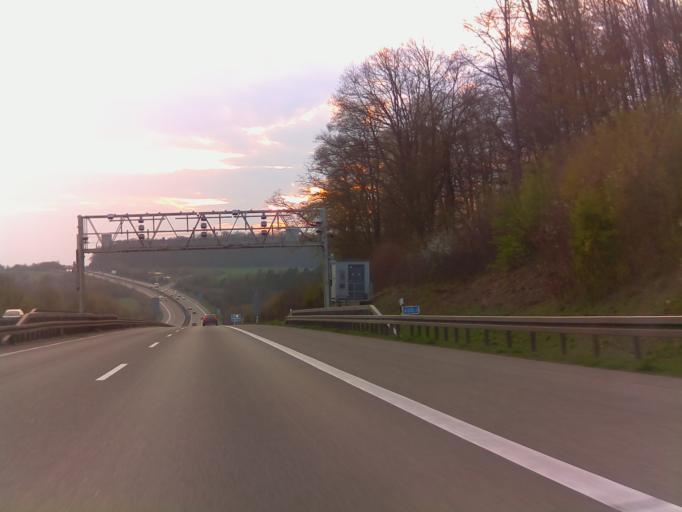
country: DE
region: Hesse
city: Kirtorf
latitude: 50.7150
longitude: 9.1286
